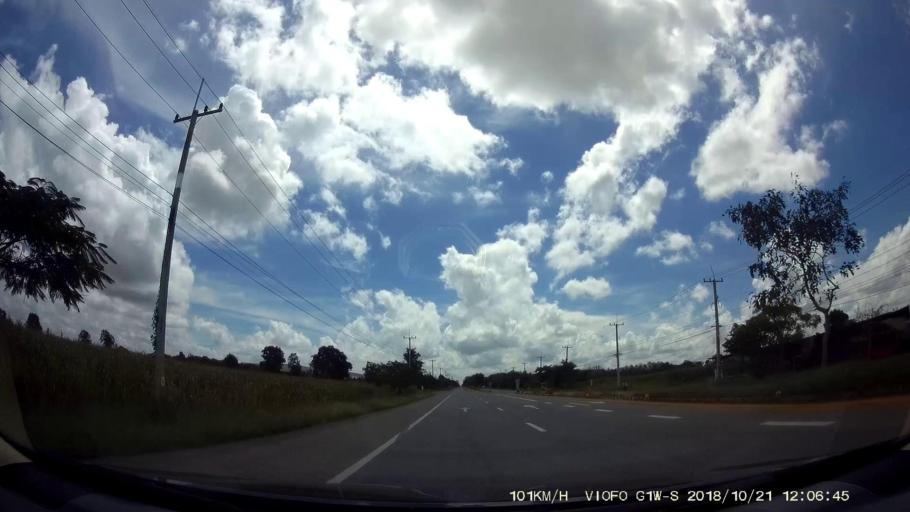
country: TH
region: Chaiyaphum
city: Chatturat
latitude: 15.4582
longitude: 101.8268
